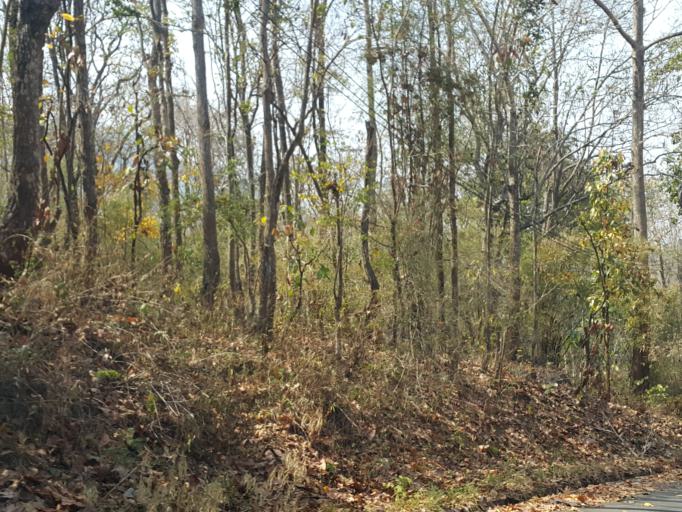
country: TH
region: Chiang Mai
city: Mae On
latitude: 18.7859
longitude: 99.2365
